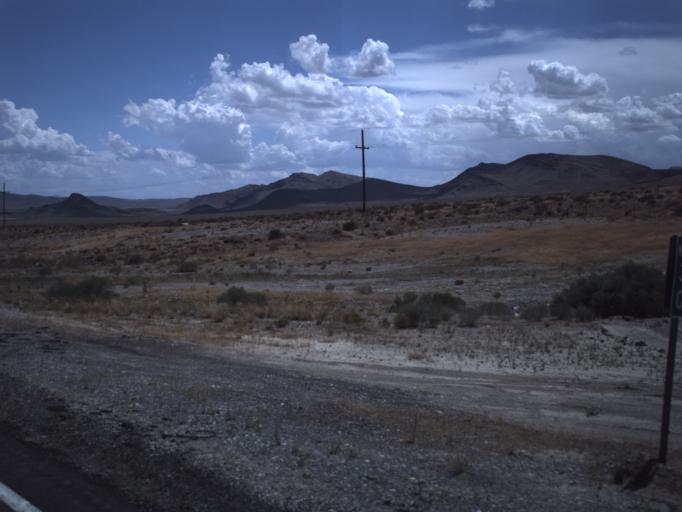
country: US
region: Utah
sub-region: Beaver County
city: Milford
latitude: 39.0848
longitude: -113.5125
